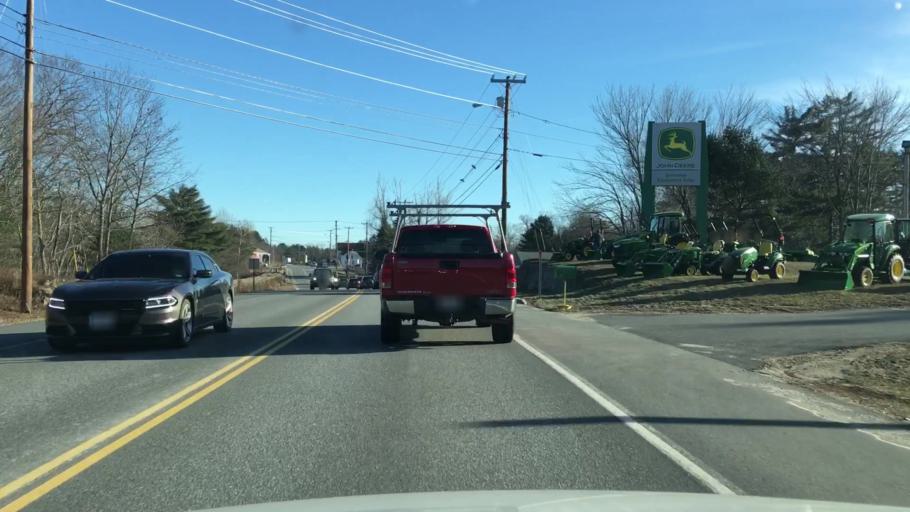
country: US
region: Maine
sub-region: Hancock County
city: Ellsworth
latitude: 44.5640
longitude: -68.4433
